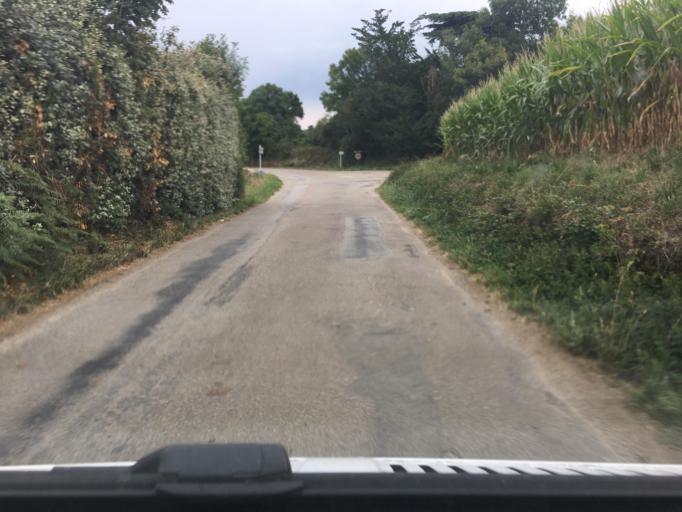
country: FR
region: Brittany
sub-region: Departement du Finistere
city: Beuzec-Cap-Sizun
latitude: 48.0825
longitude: -4.4770
